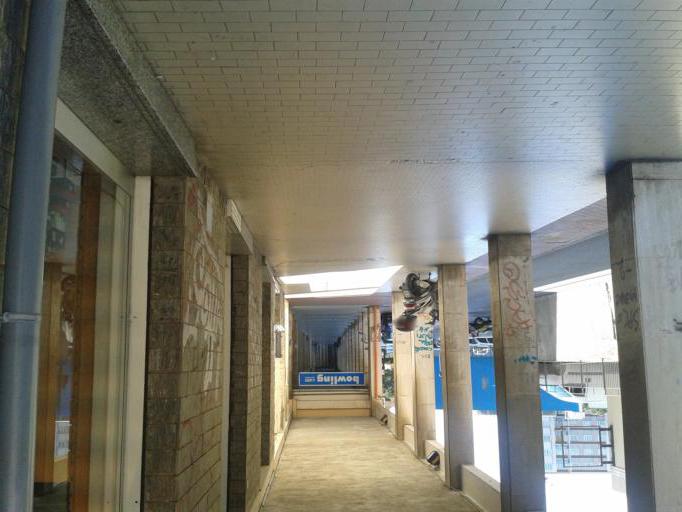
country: IT
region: Liguria
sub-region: Provincia di Savona
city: Savona
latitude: 44.3047
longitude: 8.4712
